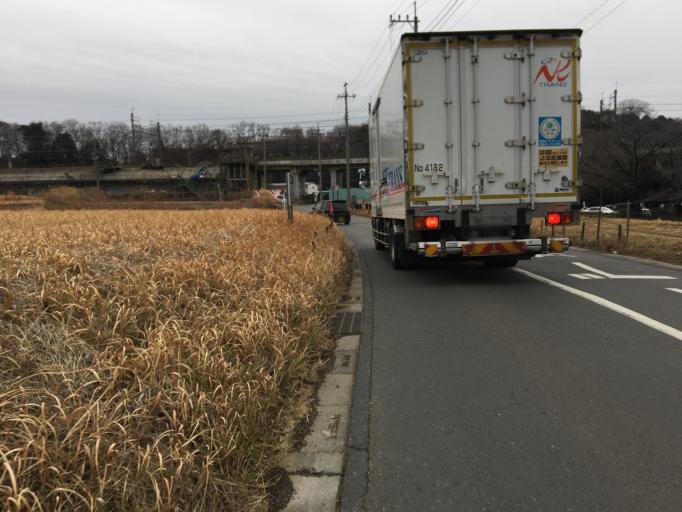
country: JP
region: Saitama
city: Oi
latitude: 35.7977
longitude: 139.5321
